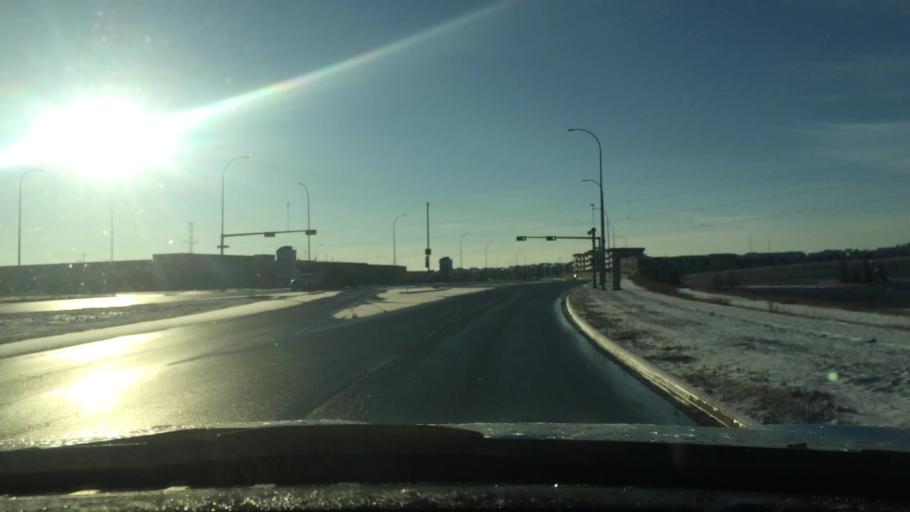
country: CA
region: Alberta
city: Calgary
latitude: 51.1713
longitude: -114.1536
